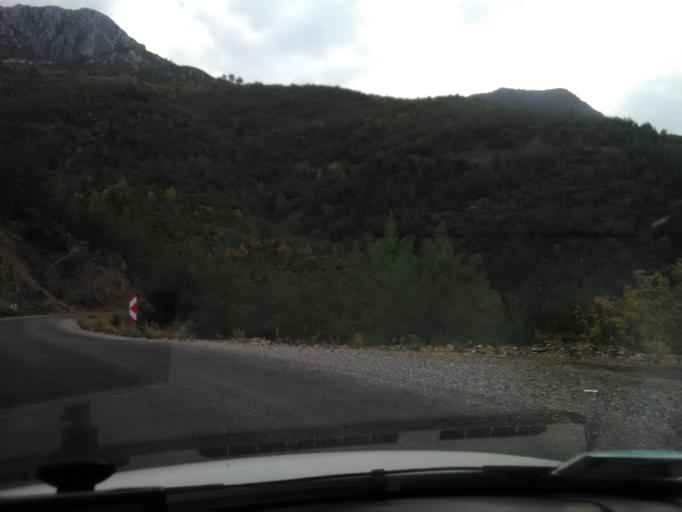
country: TR
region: Antalya
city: Gazipasa
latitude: 36.3050
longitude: 32.3945
